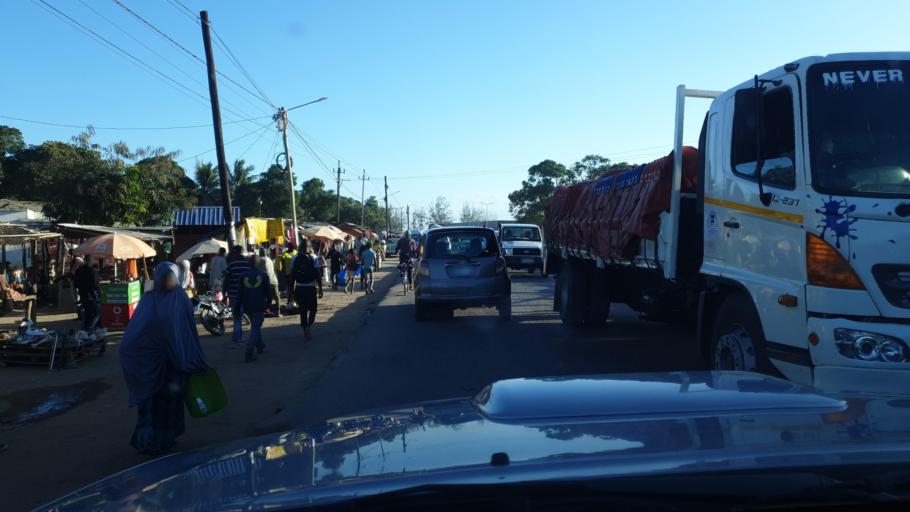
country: MZ
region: Nampula
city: Nacala
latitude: -14.5720
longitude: 40.6839
